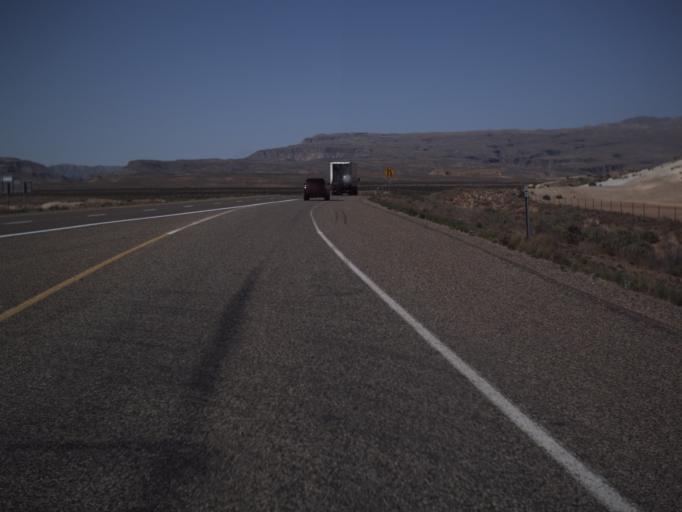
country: US
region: Utah
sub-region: Washington County
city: Saint George
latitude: 37.0009
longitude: -113.5633
